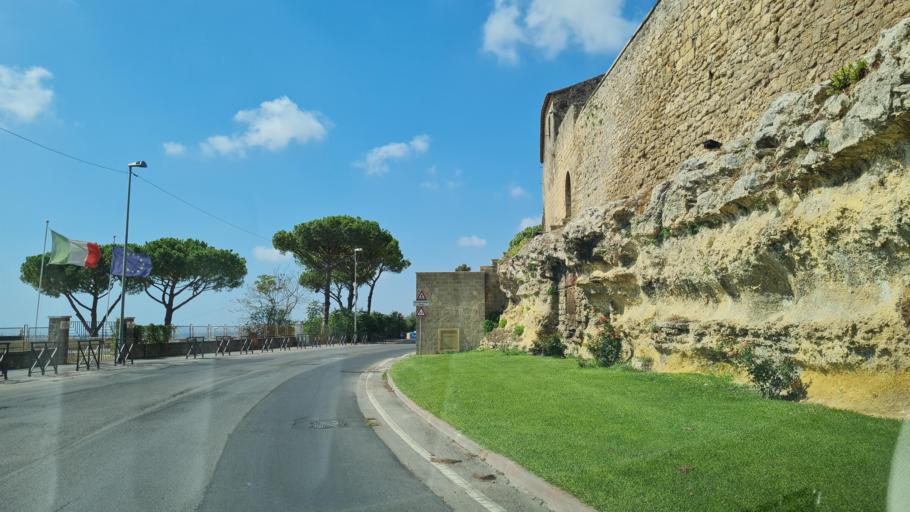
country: IT
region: Latium
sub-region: Provincia di Viterbo
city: Tarquinia
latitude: 42.2510
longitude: 11.7540
